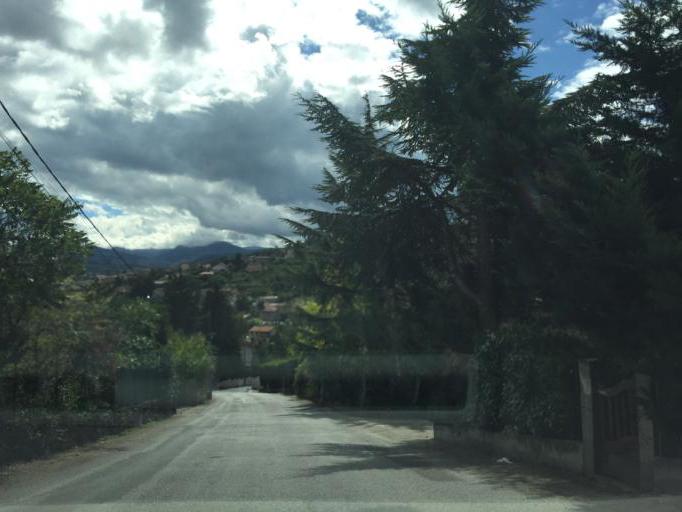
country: FR
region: Rhone-Alpes
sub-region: Departement de la Loire
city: Lorette
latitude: 45.5263
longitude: 4.5838
